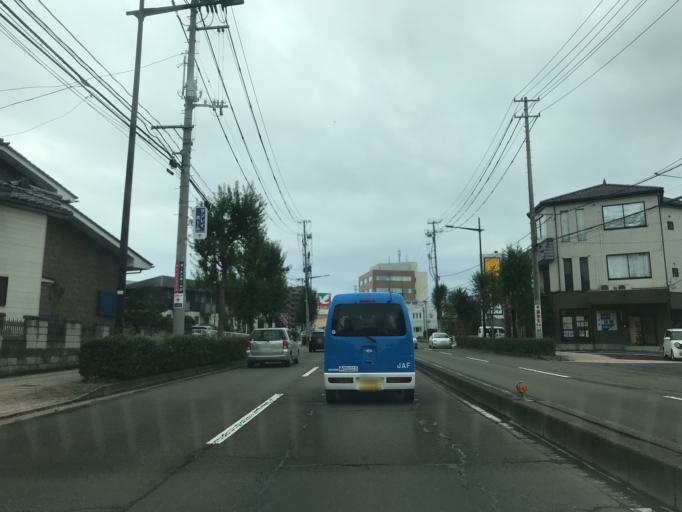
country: JP
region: Miyagi
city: Sendai-shi
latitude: 38.3125
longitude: 140.8866
